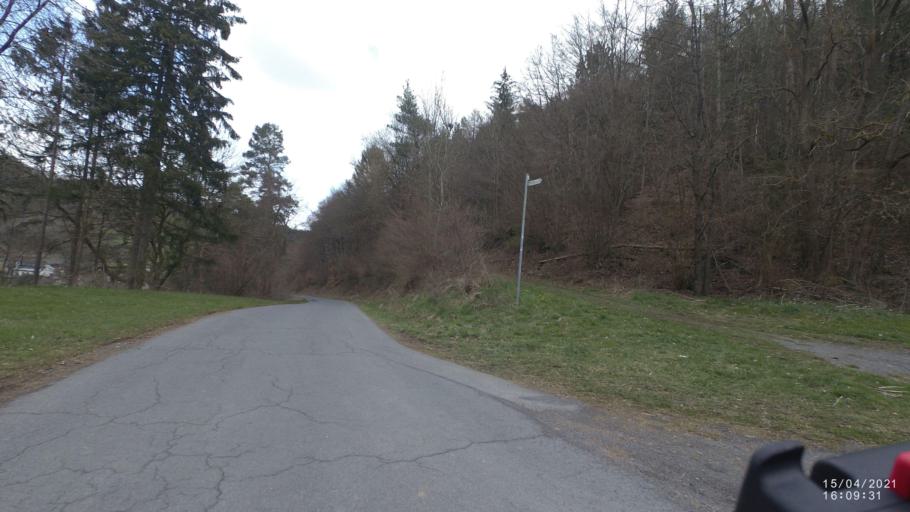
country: DE
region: Rheinland-Pfalz
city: Rieden
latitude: 50.3934
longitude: 7.1822
